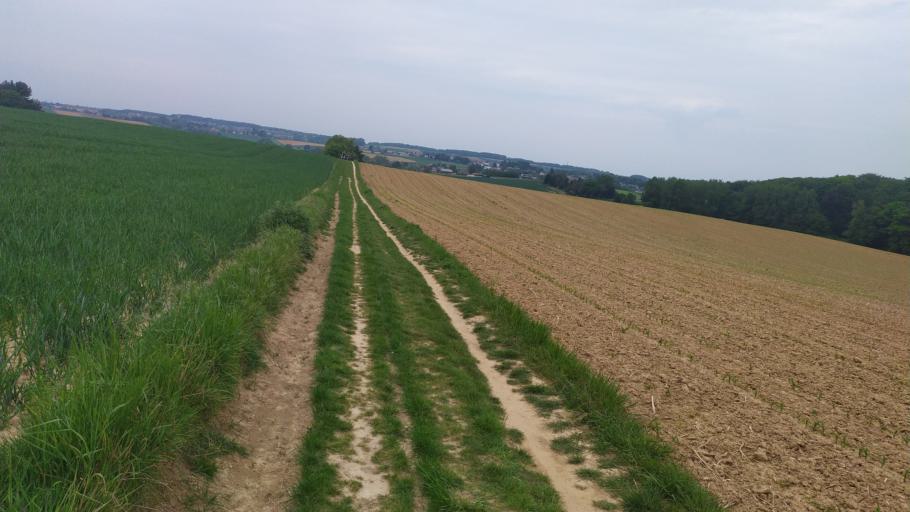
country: BE
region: Flanders
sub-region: Provincie Vlaams-Brabant
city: Huldenberg
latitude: 50.8334
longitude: 4.5898
